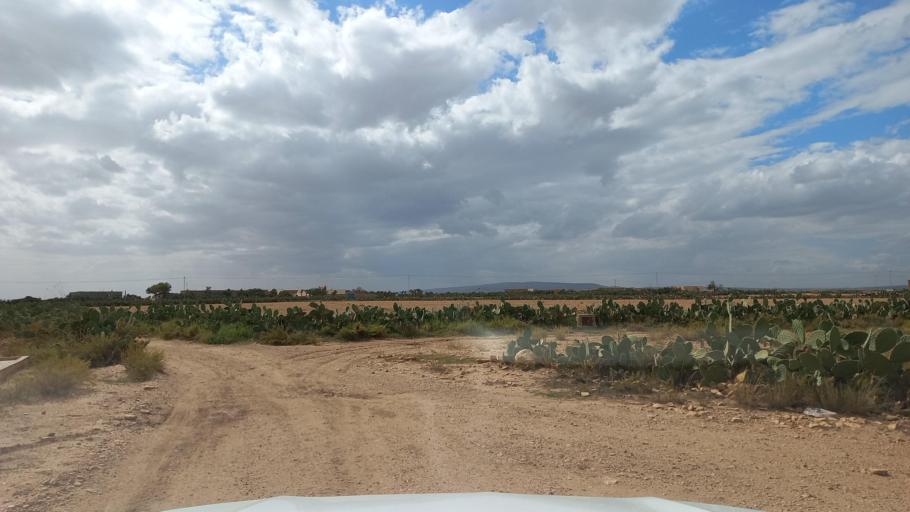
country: TN
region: Al Qasrayn
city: Sbiba
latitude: 35.3831
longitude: 9.0951
